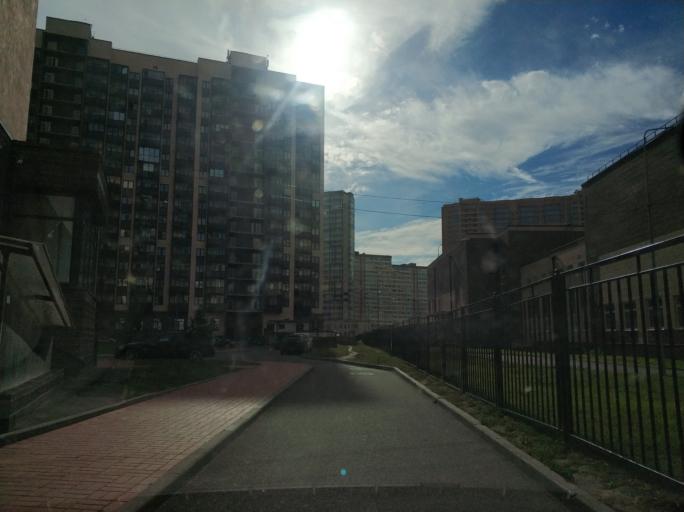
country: RU
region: Leningrad
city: Murino
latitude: 60.0512
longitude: 30.4290
